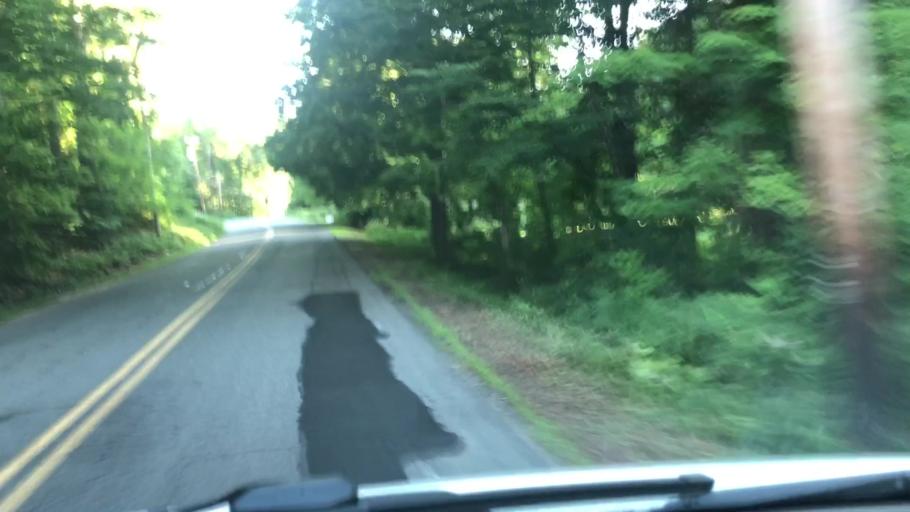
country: US
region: Massachusetts
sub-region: Hampshire County
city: Williamsburg
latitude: 42.3772
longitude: -72.7310
